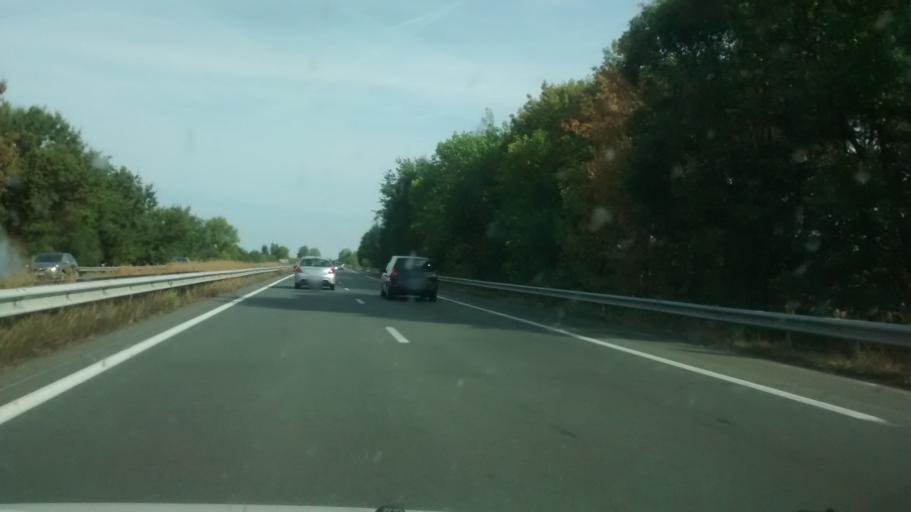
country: FR
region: Aquitaine
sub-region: Departement du Lot-et-Garonne
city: Damazan
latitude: 44.3050
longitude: 0.2599
